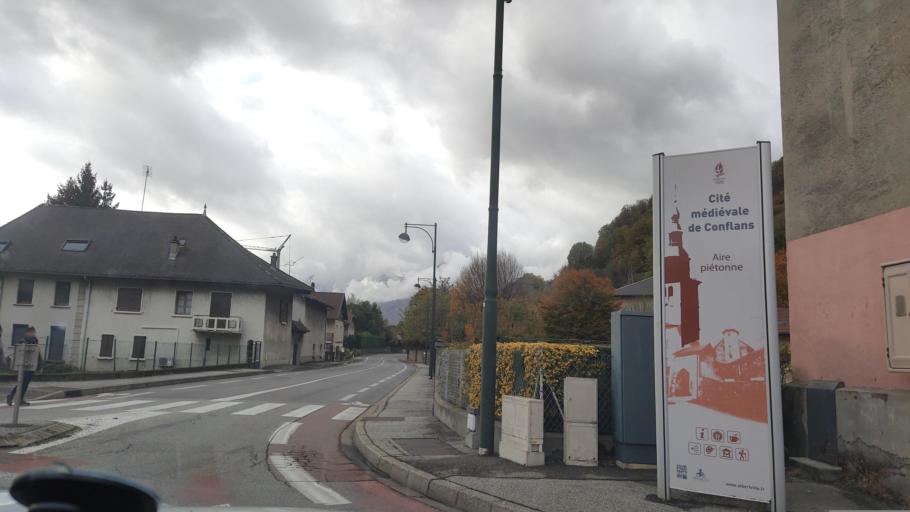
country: FR
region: Rhone-Alpes
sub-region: Departement de la Savoie
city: Albertville
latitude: 45.6687
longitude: 6.4064
